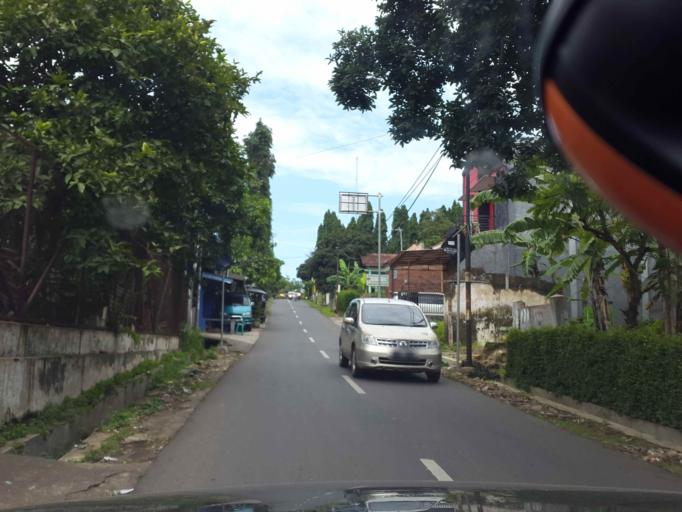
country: ID
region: Central Java
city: Salatiga
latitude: -7.3102
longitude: 110.4906
